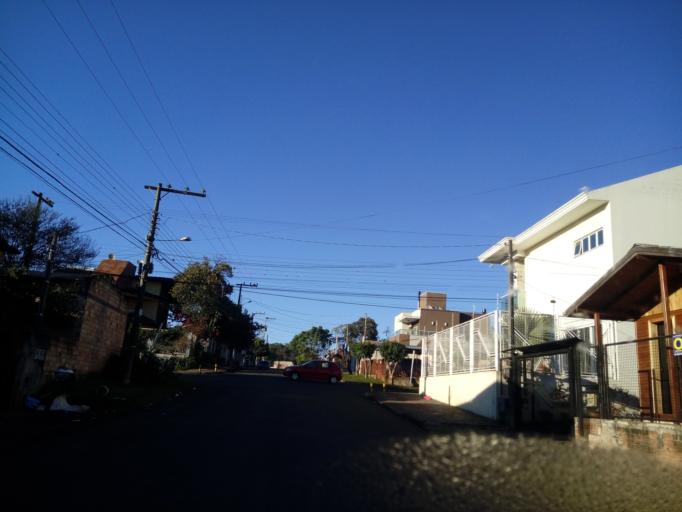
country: BR
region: Santa Catarina
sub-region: Chapeco
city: Chapeco
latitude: -27.1171
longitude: -52.6184
